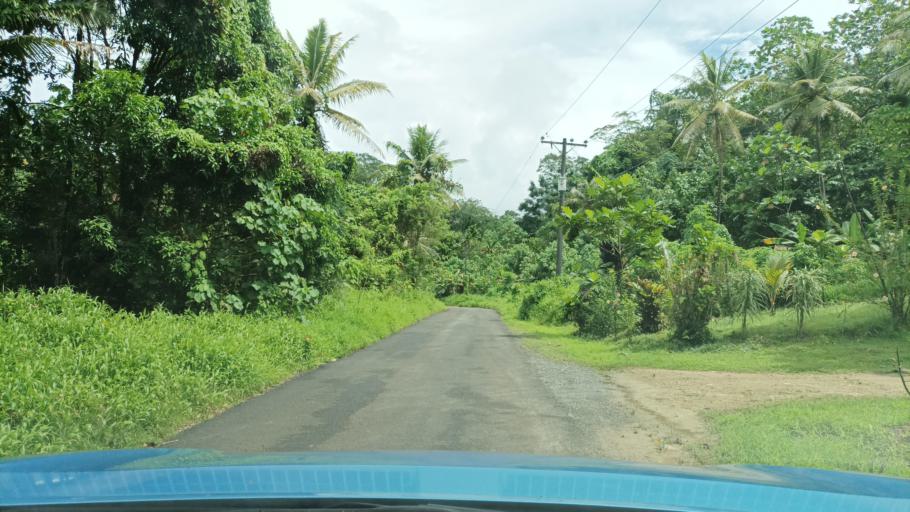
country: FM
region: Pohnpei
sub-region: Madolenihm Municipality
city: Madolenihm Municipality Government
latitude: 6.8952
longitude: 158.3162
